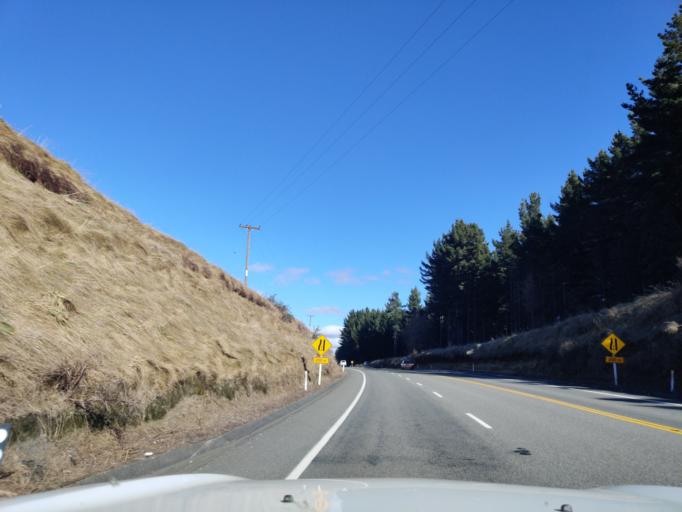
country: NZ
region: Manawatu-Wanganui
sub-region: Ruapehu District
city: Waiouru
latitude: -39.4489
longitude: 175.6788
